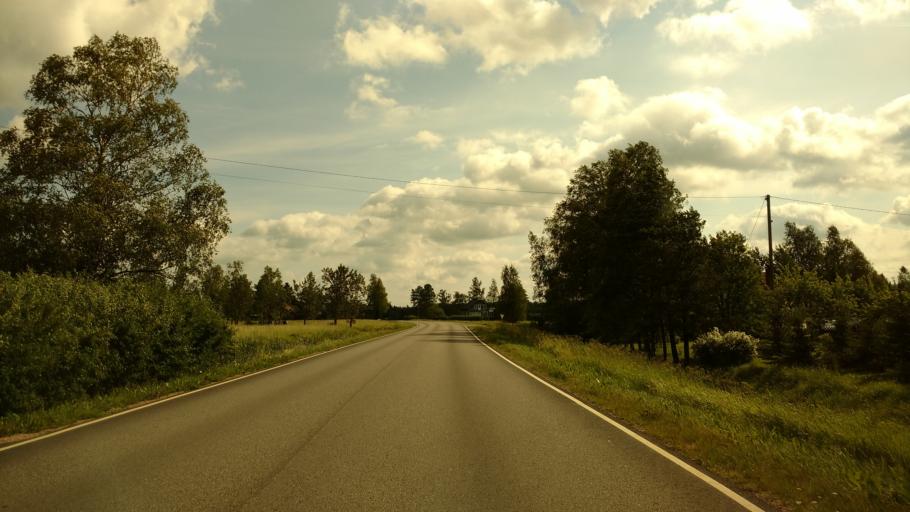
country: FI
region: Varsinais-Suomi
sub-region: Loimaa
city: Koski Tl
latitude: 60.6436
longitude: 23.1133
